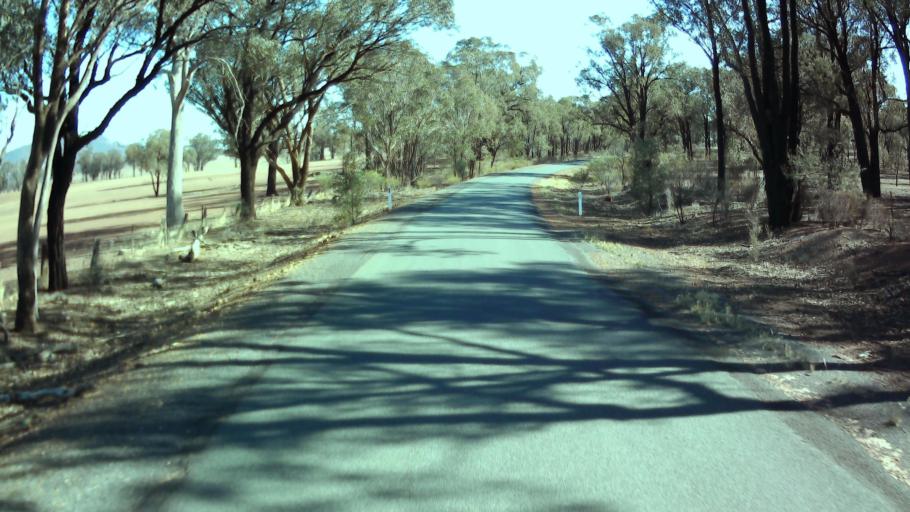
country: AU
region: New South Wales
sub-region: Weddin
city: Grenfell
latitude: -33.7856
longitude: 147.9584
